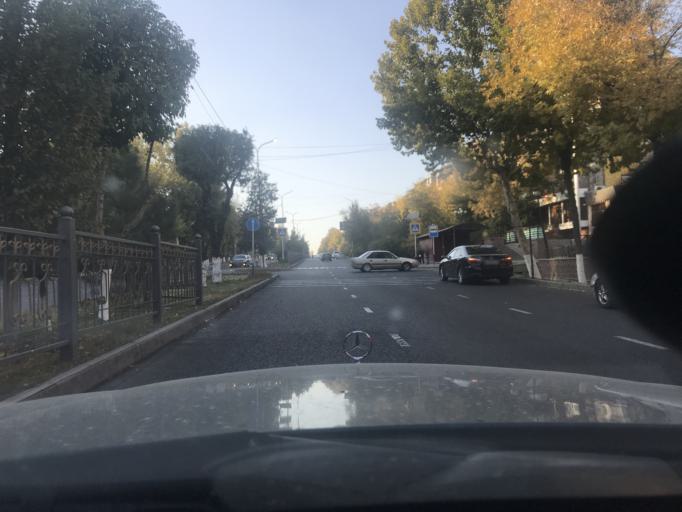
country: KZ
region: Ongtustik Qazaqstan
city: Shymkent
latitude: 42.3013
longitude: 69.6067
